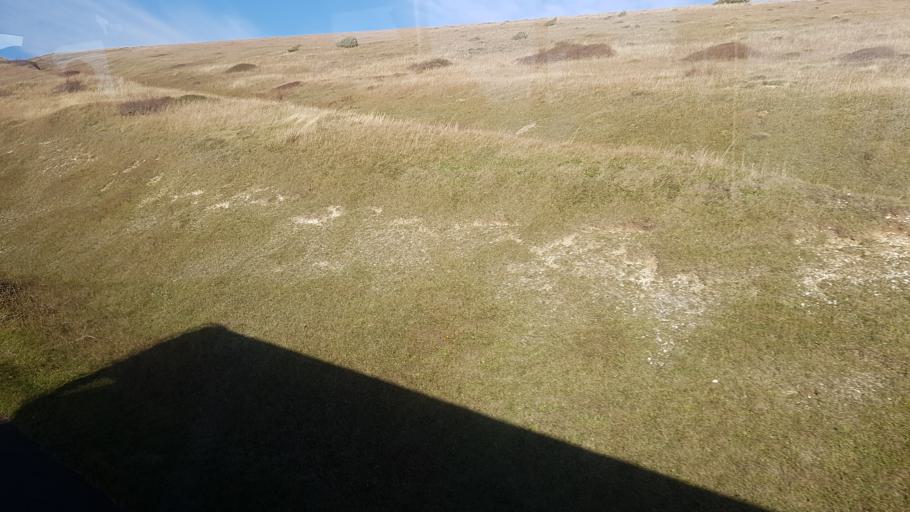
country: GB
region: England
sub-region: Isle of Wight
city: Freshwater
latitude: 50.6676
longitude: -1.4855
